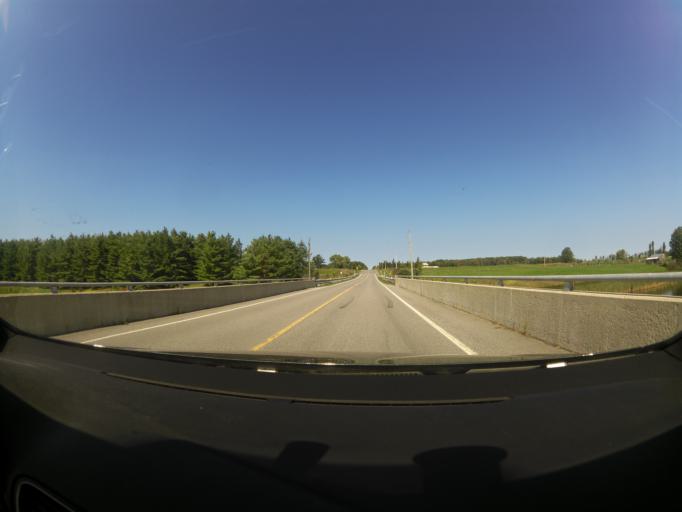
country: CA
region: Ontario
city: Arnprior
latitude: 45.3776
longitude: -76.2662
